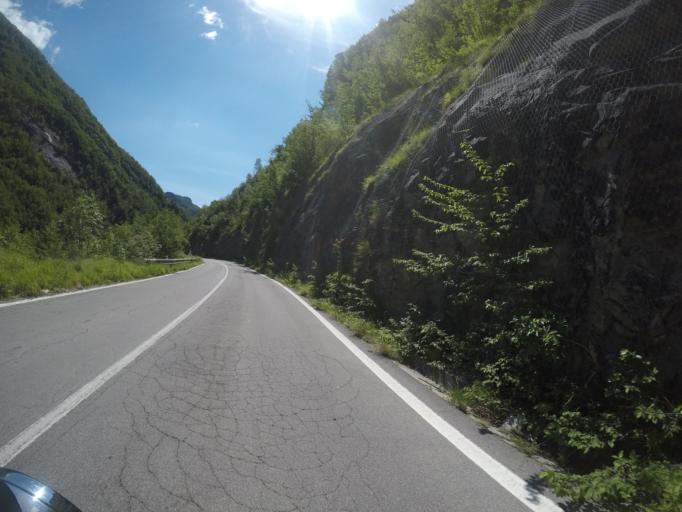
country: IT
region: Tuscany
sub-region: Provincia di Lucca
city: Fontana delle Monache
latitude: 44.0622
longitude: 10.2912
